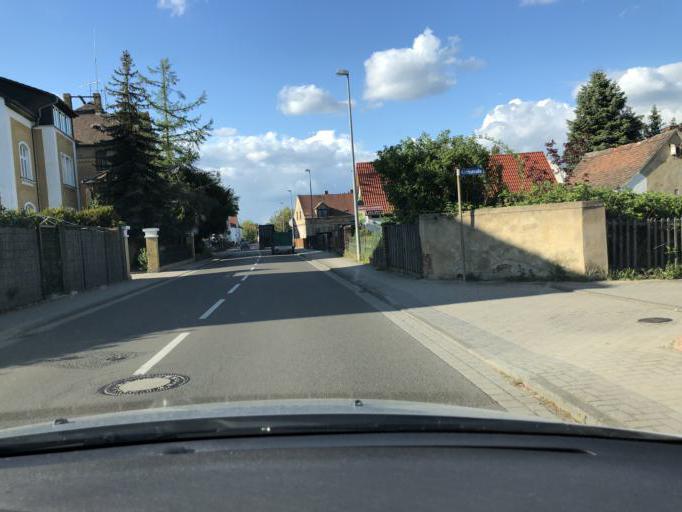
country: DE
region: Saxony
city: Bohlen
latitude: 51.2355
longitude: 12.3850
